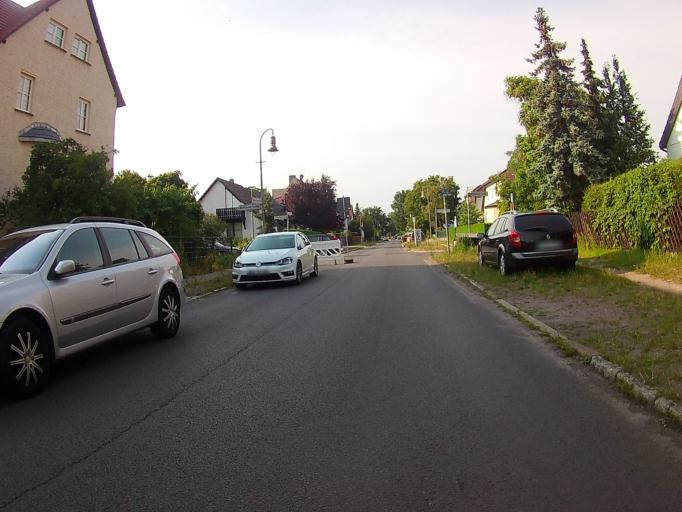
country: DE
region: Berlin
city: Kopenick Bezirk
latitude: 52.4627
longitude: 13.5719
